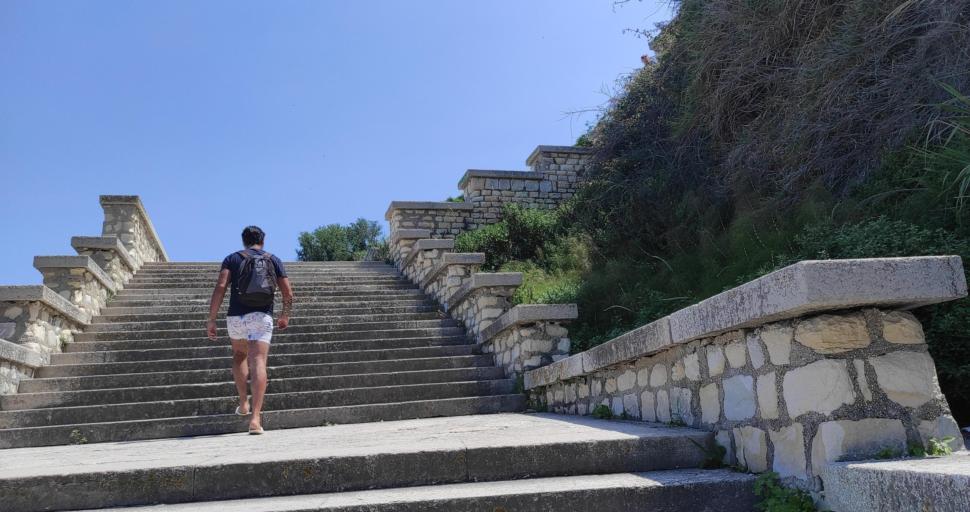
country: IT
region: The Marches
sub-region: Provincia di Ancona
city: Pietra la Croce
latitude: 43.6156
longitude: 13.5343
